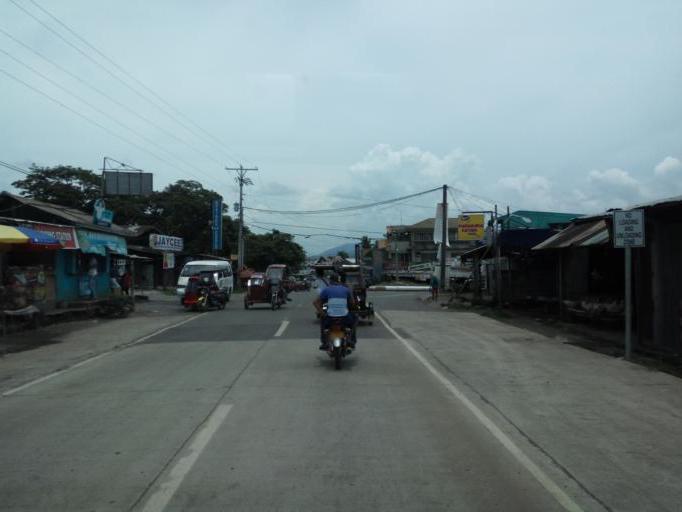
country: PH
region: Cagayan Valley
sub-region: Province of Quirino
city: Saguday
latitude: 16.5192
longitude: 121.5233
